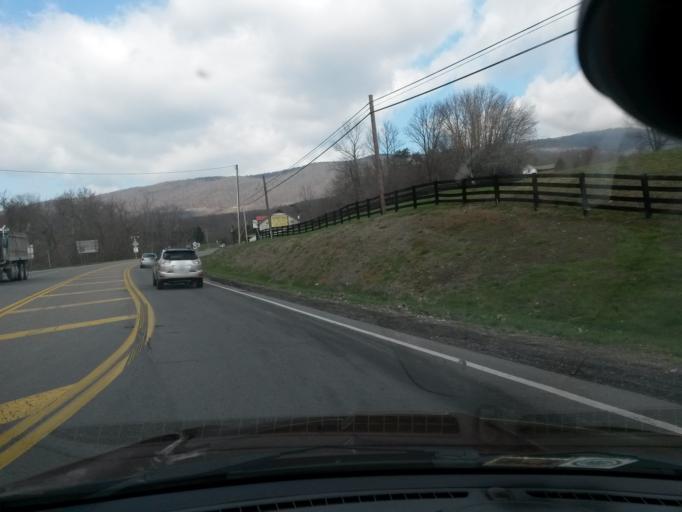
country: US
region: Virginia
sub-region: City of Waynesboro
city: Waynesboro
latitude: 38.0299
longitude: -78.8071
